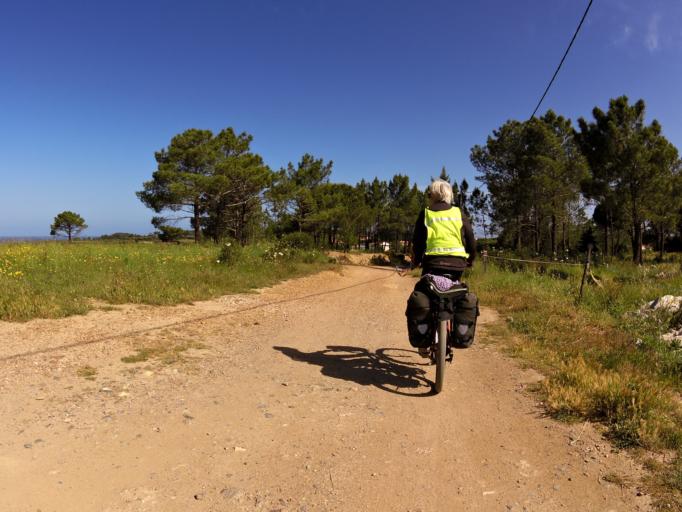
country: PT
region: Faro
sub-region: Aljezur
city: Aljezur
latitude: 37.3340
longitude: -8.8087
